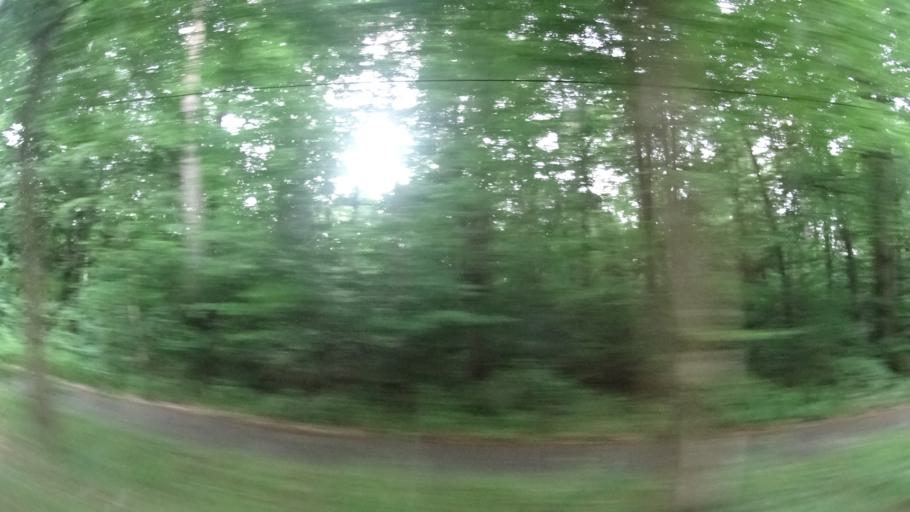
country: DE
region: Rheinland-Pfalz
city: Schifferstadt
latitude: 49.3524
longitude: 8.3866
